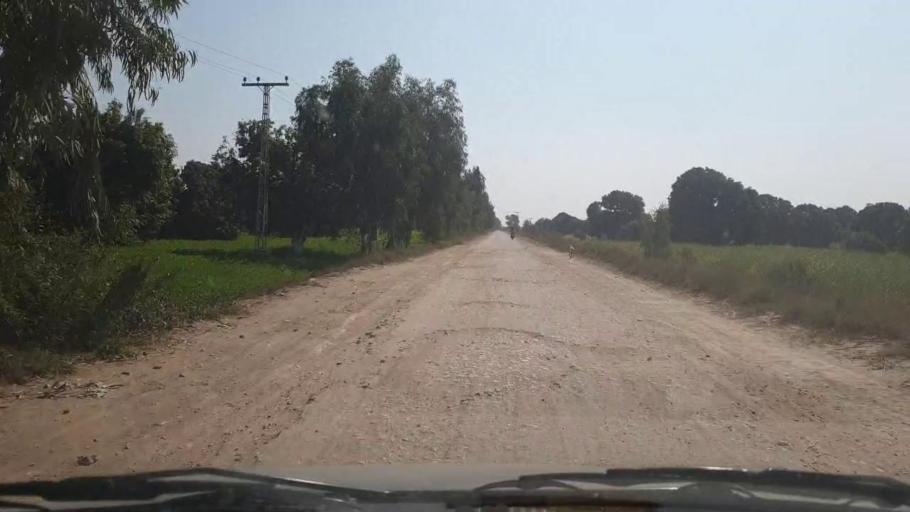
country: PK
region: Sindh
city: Samaro
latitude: 25.2683
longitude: 69.3472
